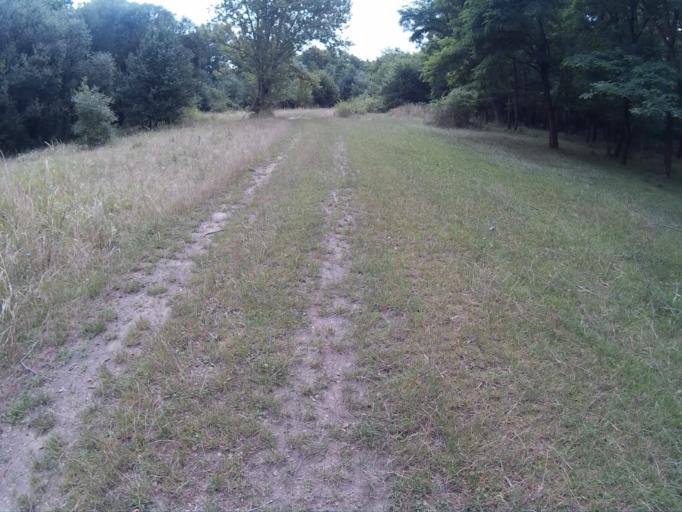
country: HU
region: Veszprem
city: Papa
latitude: 47.2803
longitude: 17.5723
